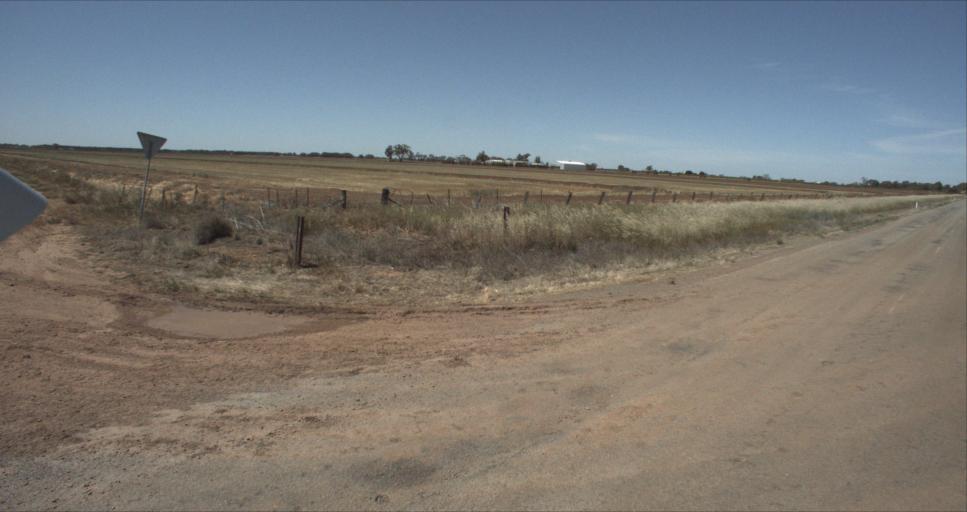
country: AU
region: New South Wales
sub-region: Leeton
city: Leeton
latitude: -34.5141
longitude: 146.2845
